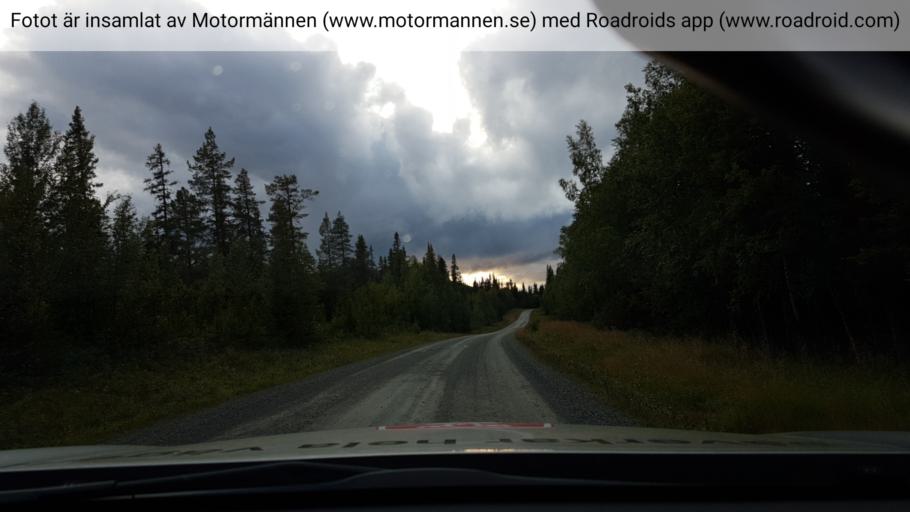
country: SE
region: Vaesterbotten
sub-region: Vilhelmina Kommun
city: Sjoberg
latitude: 65.5062
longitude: 15.6472
